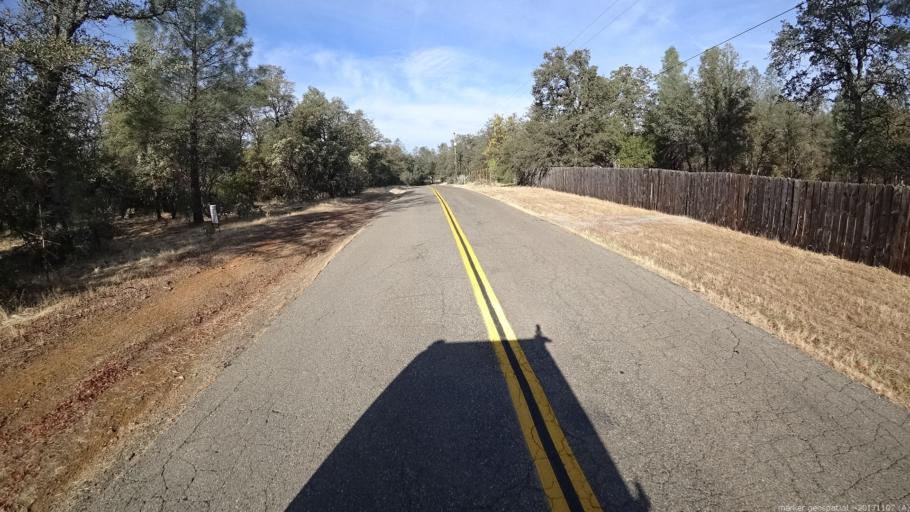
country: US
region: California
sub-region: Shasta County
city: Redding
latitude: 40.5510
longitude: -122.4420
